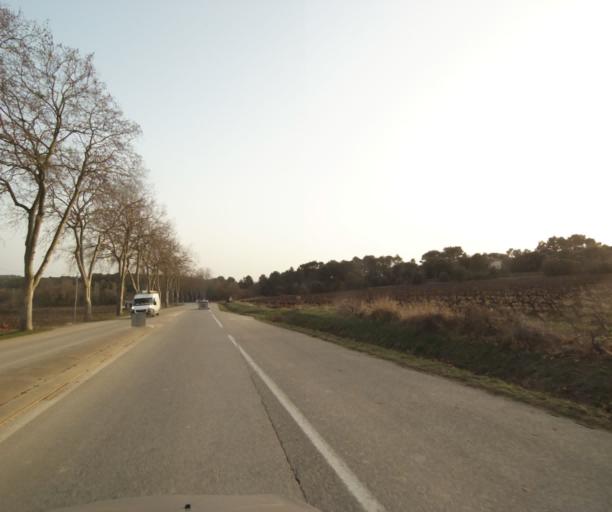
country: FR
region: Provence-Alpes-Cote d'Azur
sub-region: Departement des Bouches-du-Rhone
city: Rognes
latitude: 43.6468
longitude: 5.3583
